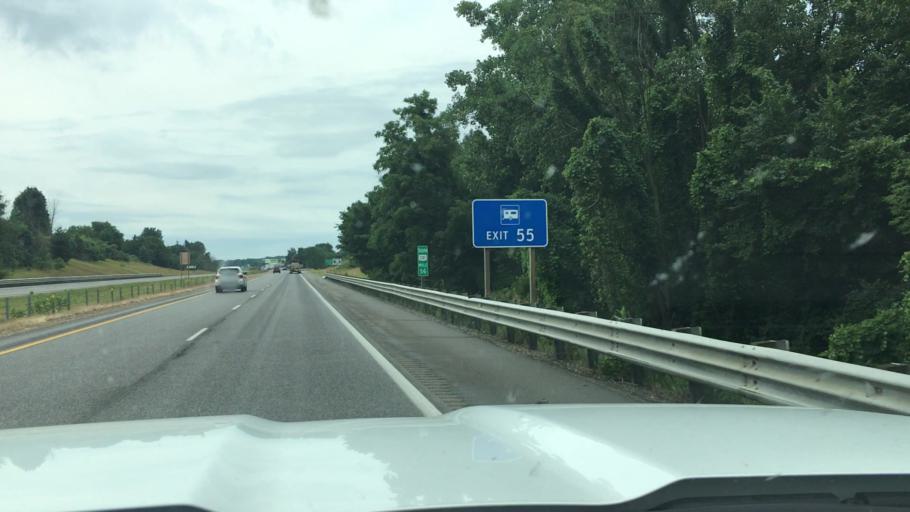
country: US
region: Michigan
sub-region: Allegan County
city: Otsego
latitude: 42.5519
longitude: -85.6623
